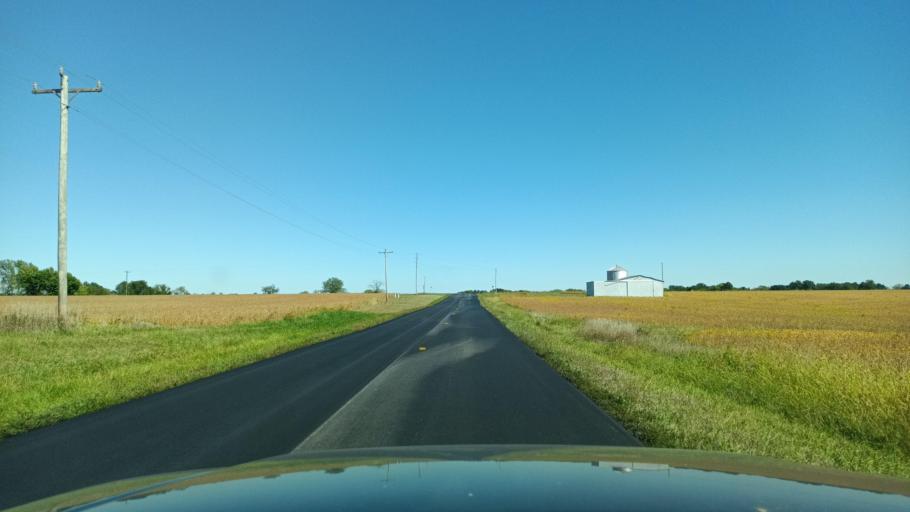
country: US
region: Missouri
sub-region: Macon County
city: La Plata
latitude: 39.9274
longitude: -92.5533
